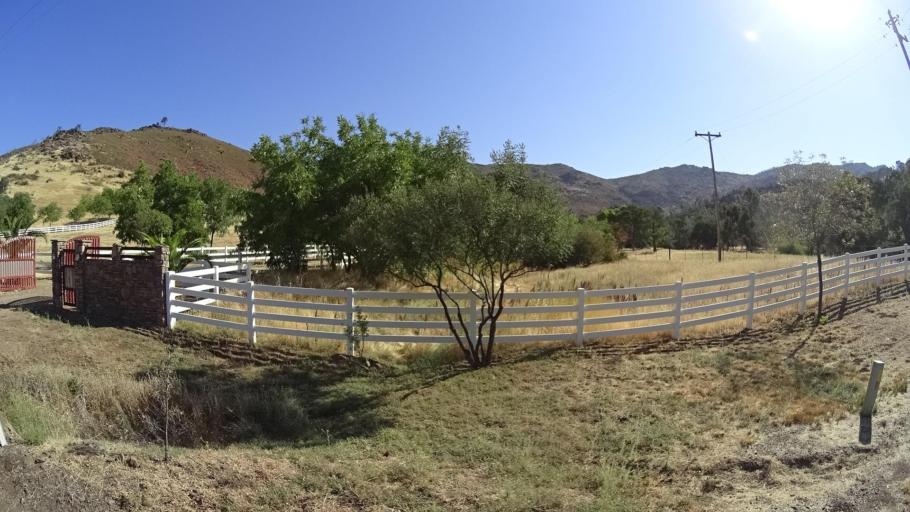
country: US
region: California
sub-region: Mariposa County
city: Mariposa
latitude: 37.6024
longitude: -120.1927
